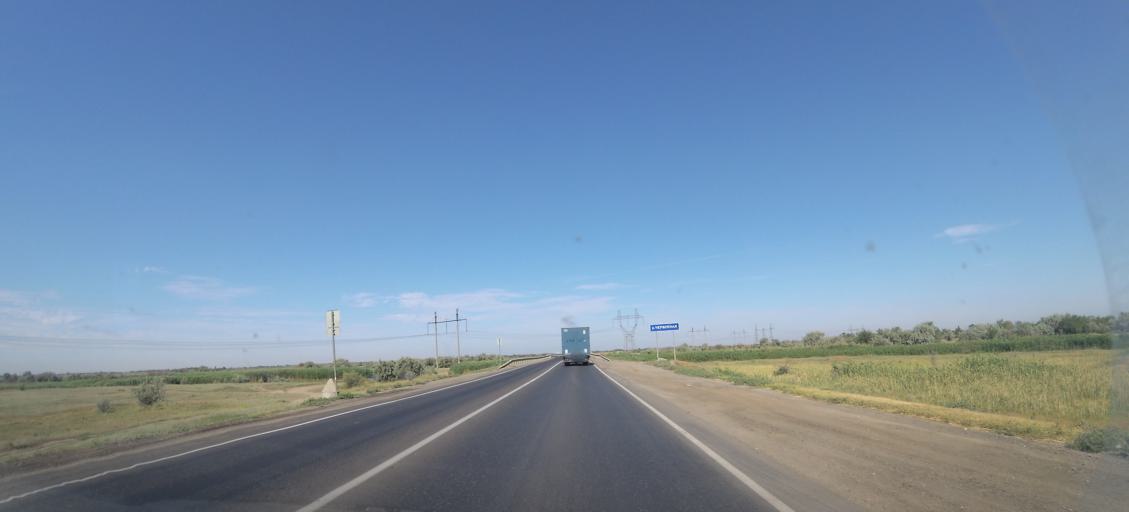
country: RU
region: Volgograd
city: Novyy Rogachik
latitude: 48.6803
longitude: 44.0417
